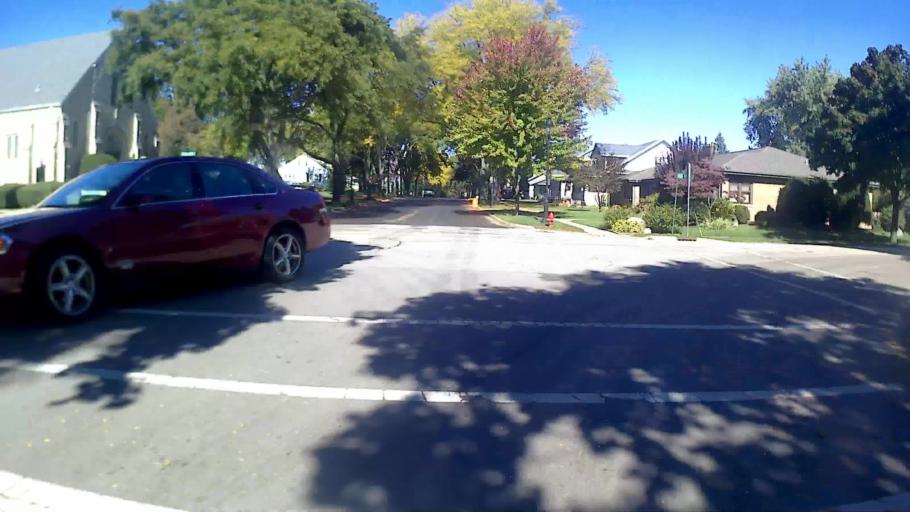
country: US
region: Illinois
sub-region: DuPage County
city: Itasca
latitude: 41.9742
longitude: -88.0130
